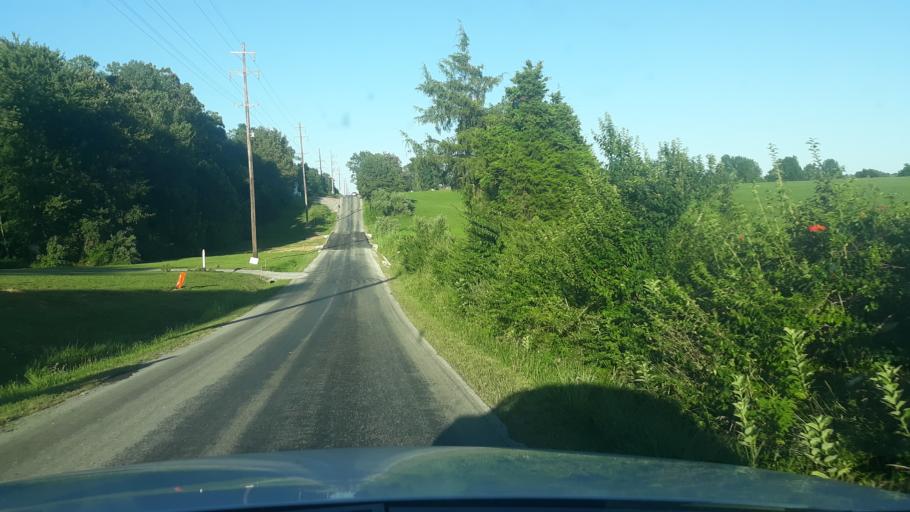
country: US
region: Illinois
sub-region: Saline County
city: Harrisburg
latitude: 37.8633
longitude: -88.6002
